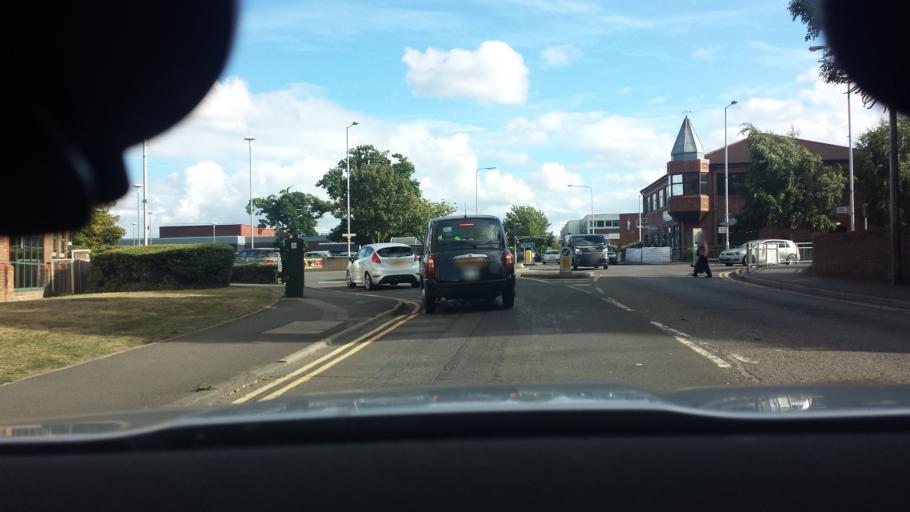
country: GB
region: England
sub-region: Kent
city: Swanley
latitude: 51.3979
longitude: 0.1721
